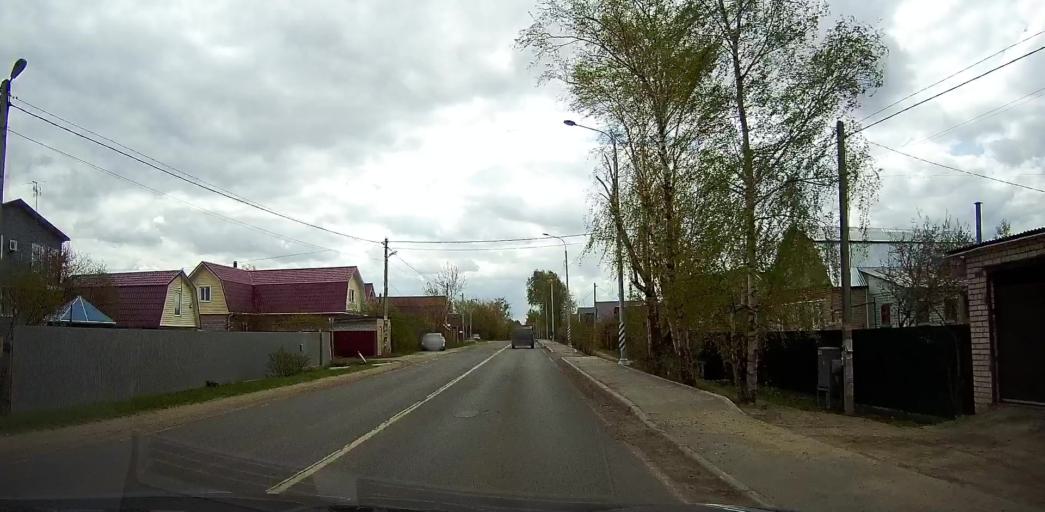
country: RU
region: Moskovskaya
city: Beloozerskiy
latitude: 55.4666
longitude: 38.4179
